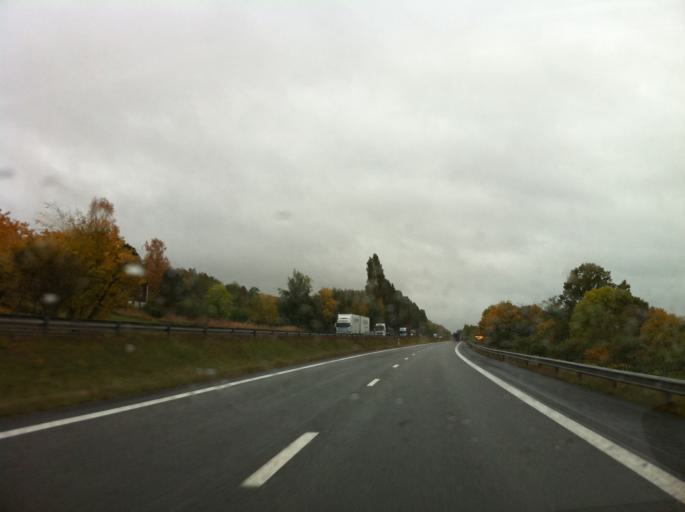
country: SE
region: Joenkoeping
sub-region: Jonkopings Kommun
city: Kaxholmen
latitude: 57.8460
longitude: 14.2676
